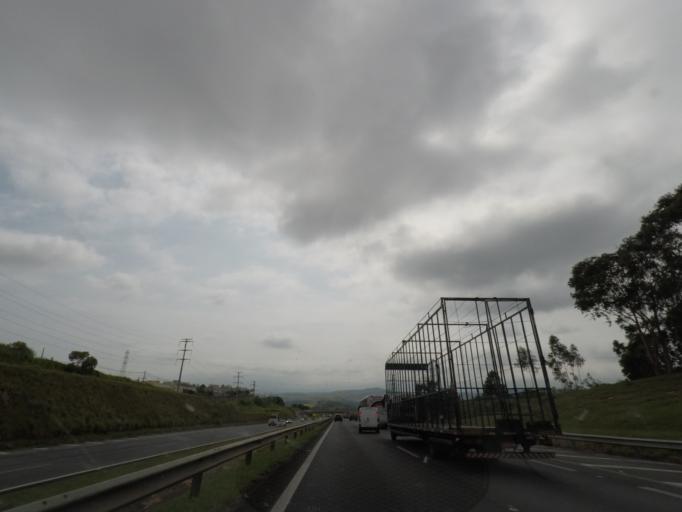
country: BR
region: Sao Paulo
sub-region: Campinas
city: Campinas
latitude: -22.9005
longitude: -46.9934
